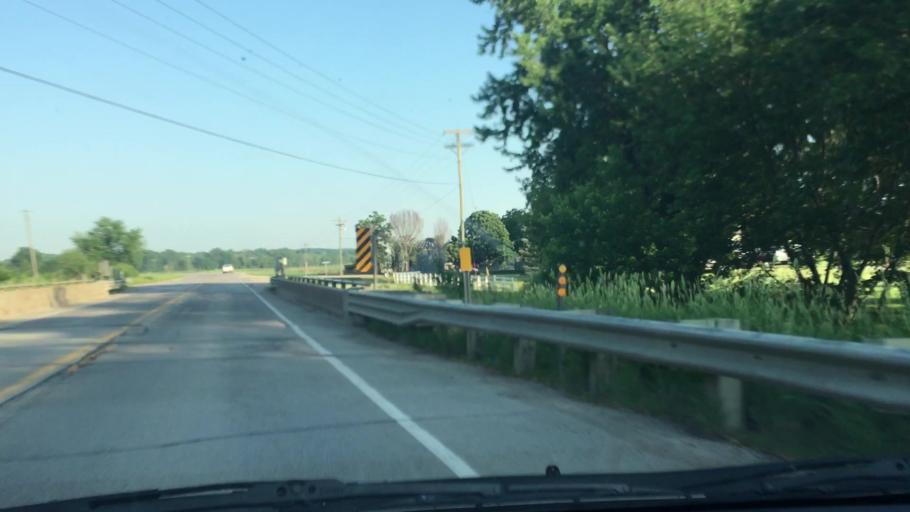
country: US
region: Iowa
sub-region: Johnson County
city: Tiffin
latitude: 41.7123
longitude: -91.6992
